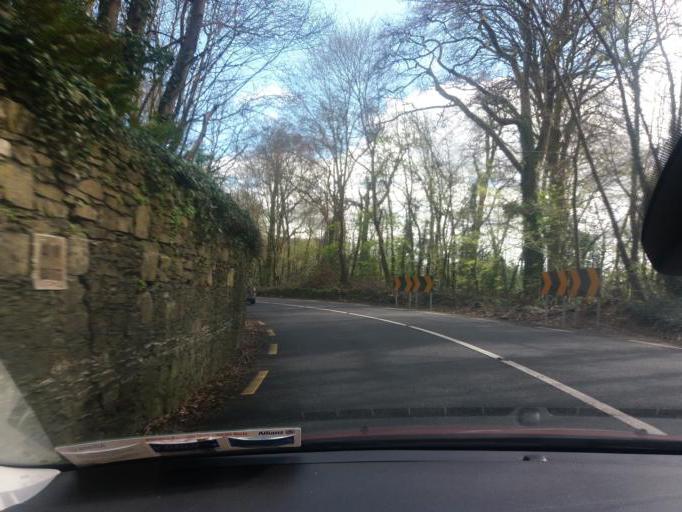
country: IE
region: Munster
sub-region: County Cork
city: Carrigtwohill
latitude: 51.8946
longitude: -8.2827
